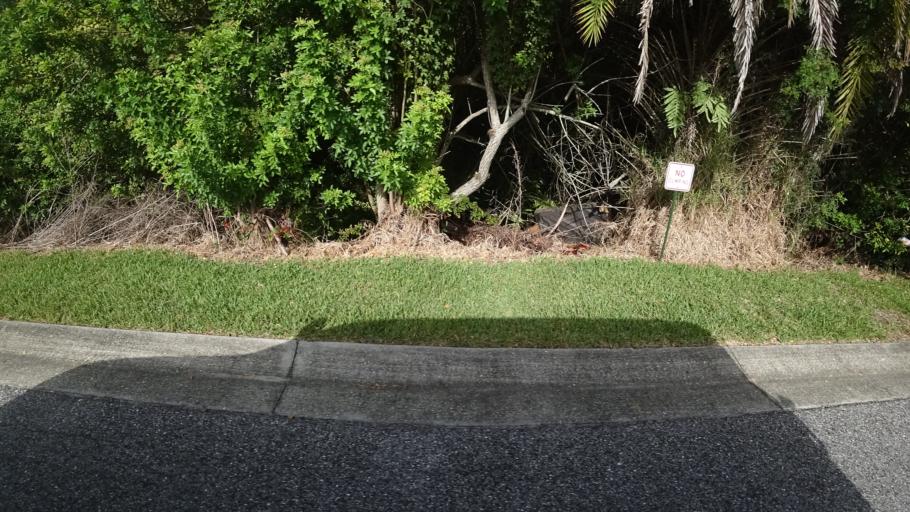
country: US
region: Florida
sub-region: Manatee County
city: Ellenton
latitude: 27.5524
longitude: -82.4978
